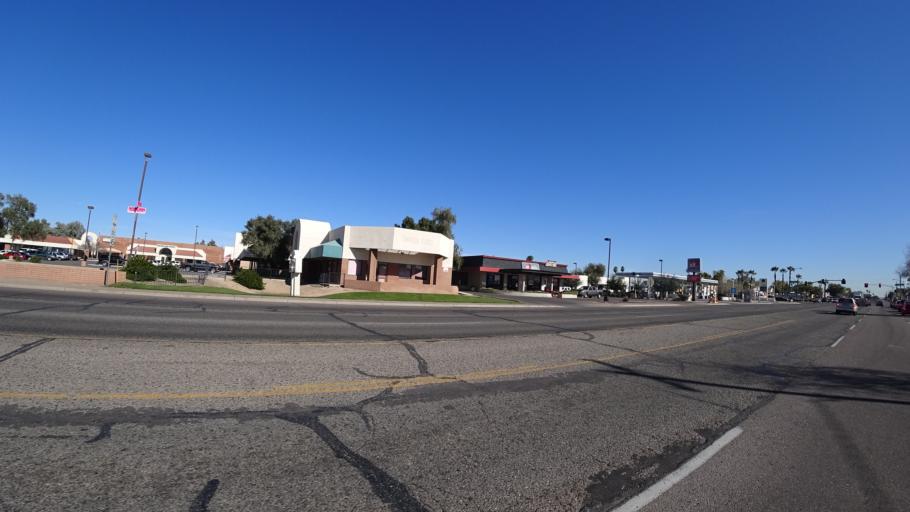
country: US
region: Arizona
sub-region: Maricopa County
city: Glendale
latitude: 33.4946
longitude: -112.2223
